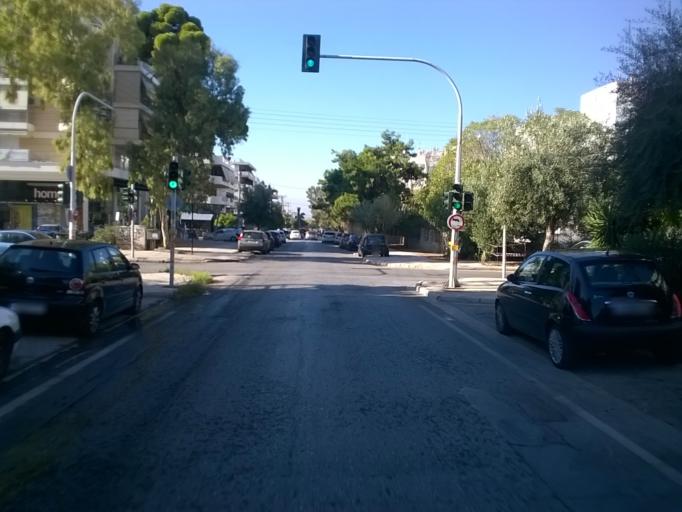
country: GR
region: Attica
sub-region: Nomarchia Athinas
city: Glyfada
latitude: 37.8651
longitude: 23.7508
